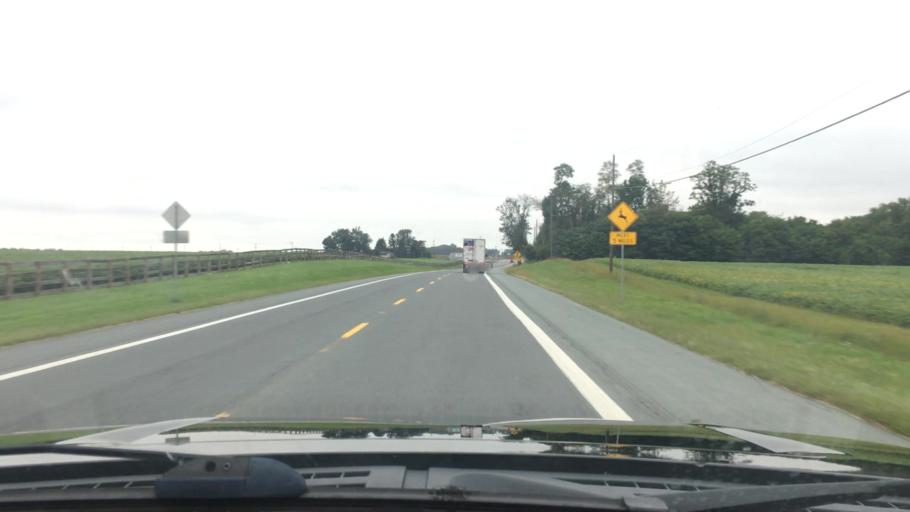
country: US
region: Maryland
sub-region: Cecil County
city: Elkton
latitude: 39.4812
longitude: -75.8481
